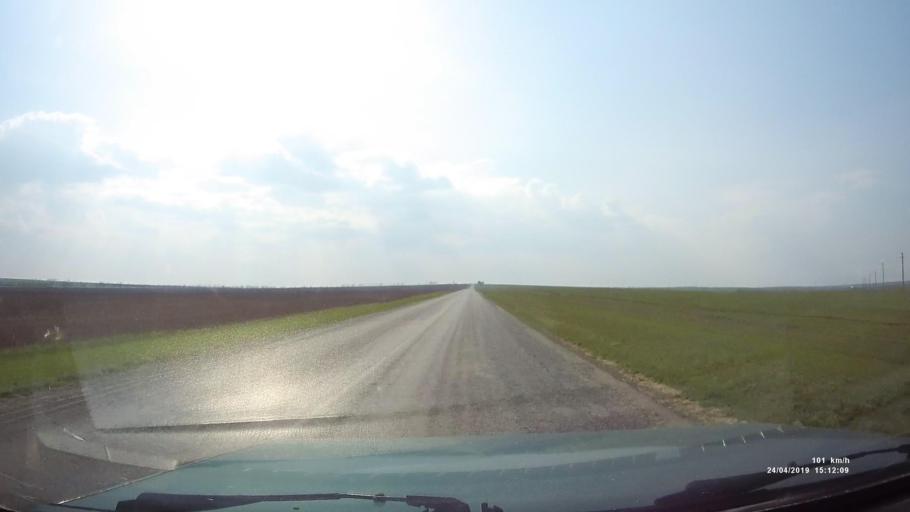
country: RU
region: Rostov
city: Remontnoye
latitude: 46.5464
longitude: 43.3069
